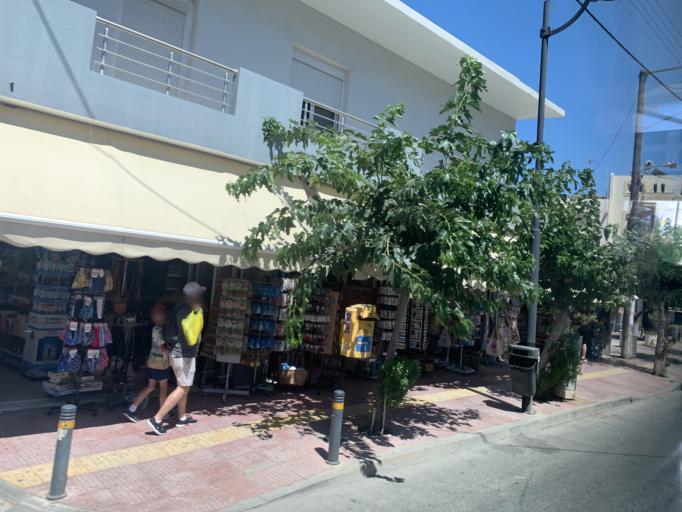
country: GR
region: Crete
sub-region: Nomos Irakleiou
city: Limin Khersonisou
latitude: 35.3170
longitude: 25.3917
